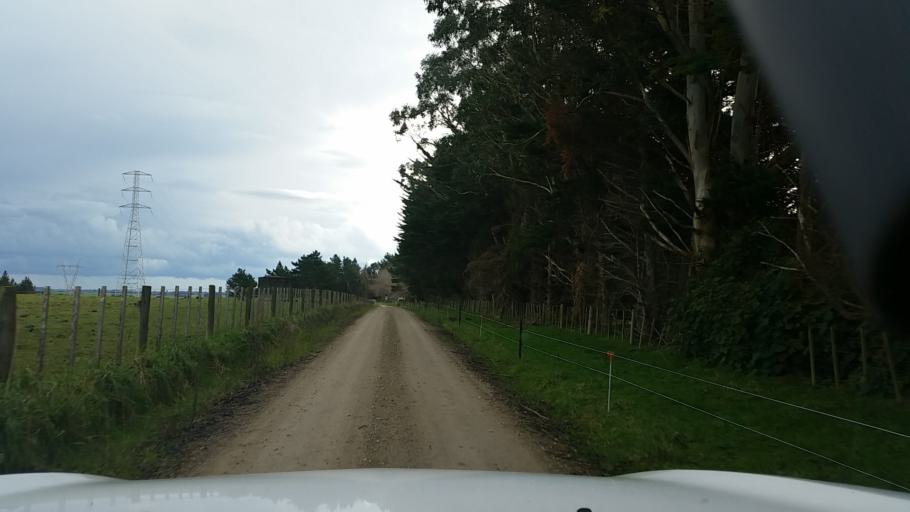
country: NZ
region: Taranaki
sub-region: South Taranaki District
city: Patea
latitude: -39.7889
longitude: 174.7462
